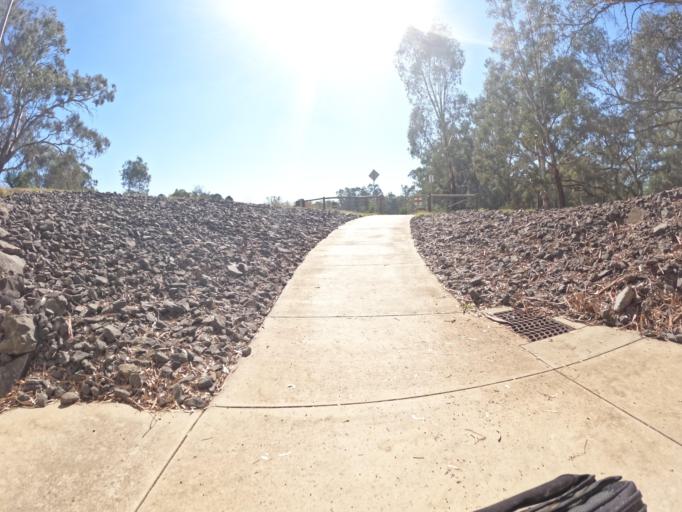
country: AU
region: Victoria
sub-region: Greater Bendigo
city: Epsom
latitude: -36.7907
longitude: 144.5075
